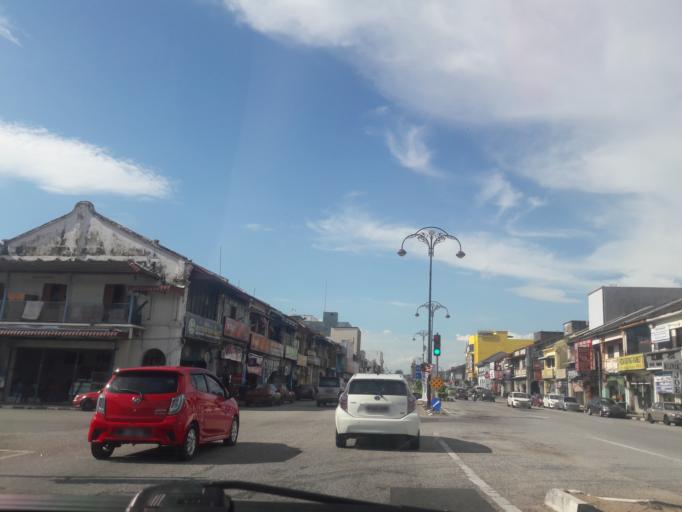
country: MY
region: Kedah
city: Sungai Petani
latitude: 5.6398
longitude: 100.4887
